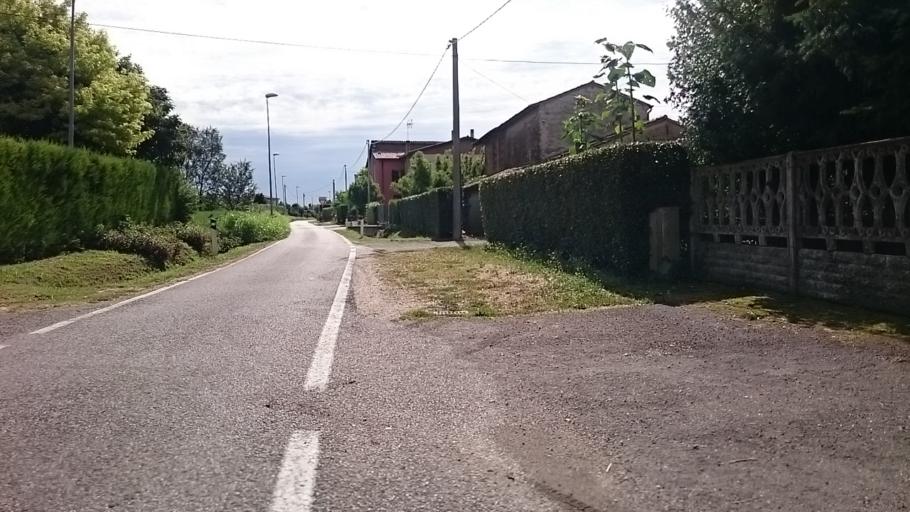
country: IT
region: Veneto
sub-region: Provincia di Padova
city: Bertipaglia
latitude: 45.3273
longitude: 11.8837
